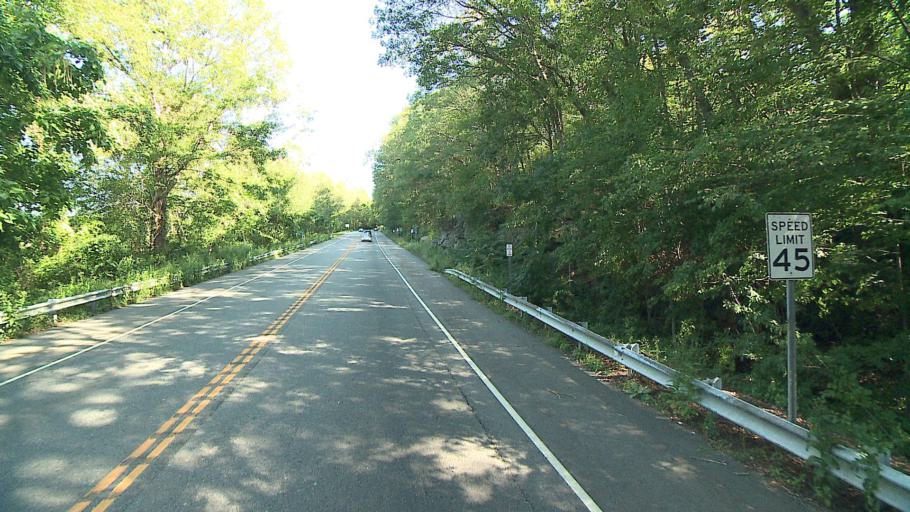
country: US
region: Connecticut
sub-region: New London County
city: Conning Towers-Nautilus Park
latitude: 41.3996
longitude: -72.0805
